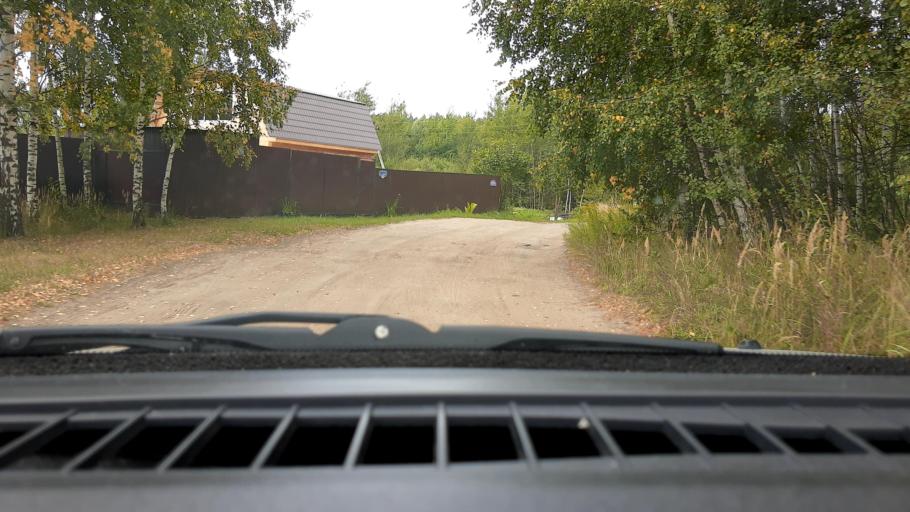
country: RU
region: Nizjnij Novgorod
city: Gorbatovka
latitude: 56.3107
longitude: 43.6903
